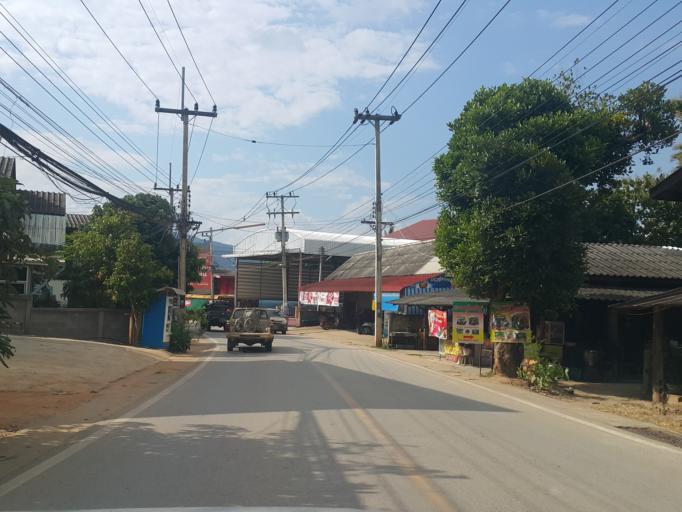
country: TH
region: Chiang Mai
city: Mae Chaem
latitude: 18.4995
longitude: 98.3683
